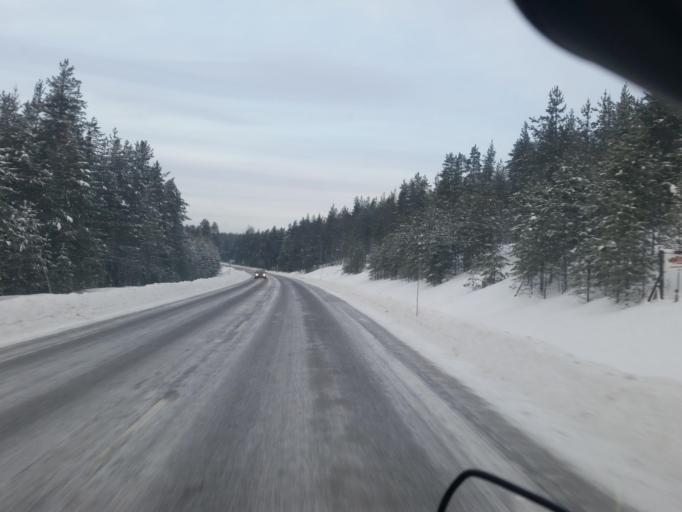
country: SE
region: Norrbotten
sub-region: Pitea Kommun
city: Pitea
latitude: 65.2629
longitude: 21.5377
